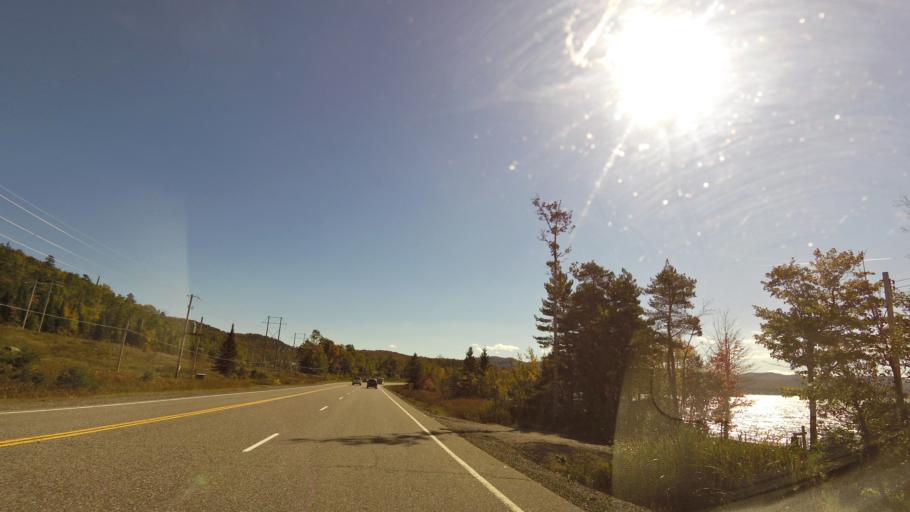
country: CA
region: Ontario
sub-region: Algoma
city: Sault Ste. Marie
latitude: 46.8939
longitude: -84.3659
